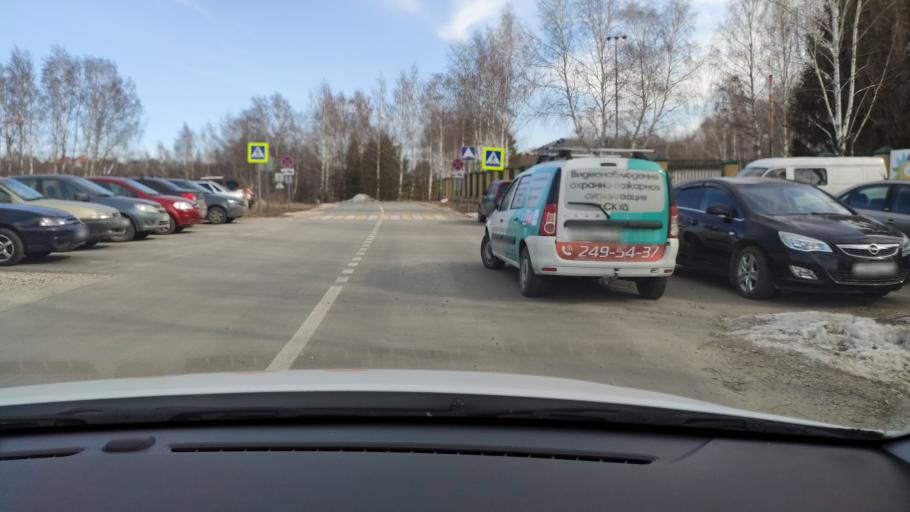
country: RU
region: Tatarstan
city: Osinovo
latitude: 55.8431
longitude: 48.9153
